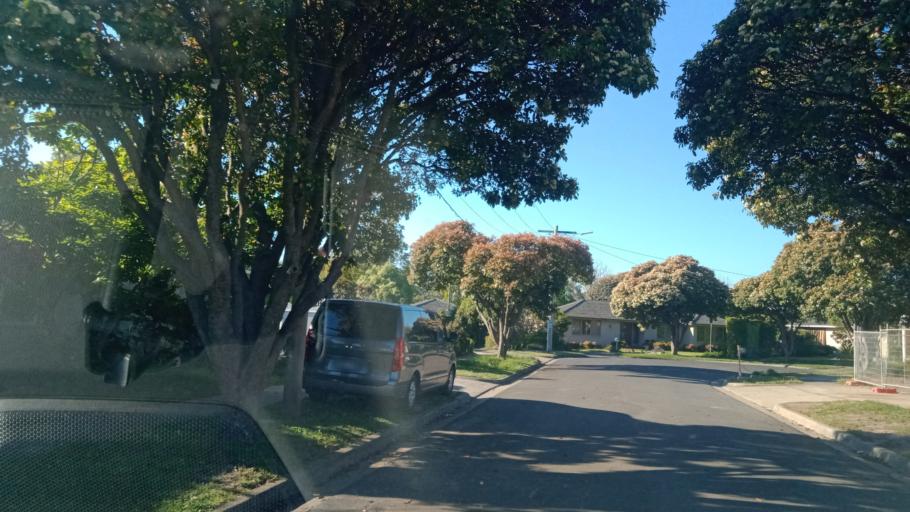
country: AU
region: Victoria
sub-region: Greater Dandenong
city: Springvale
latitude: -37.9267
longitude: 145.1692
